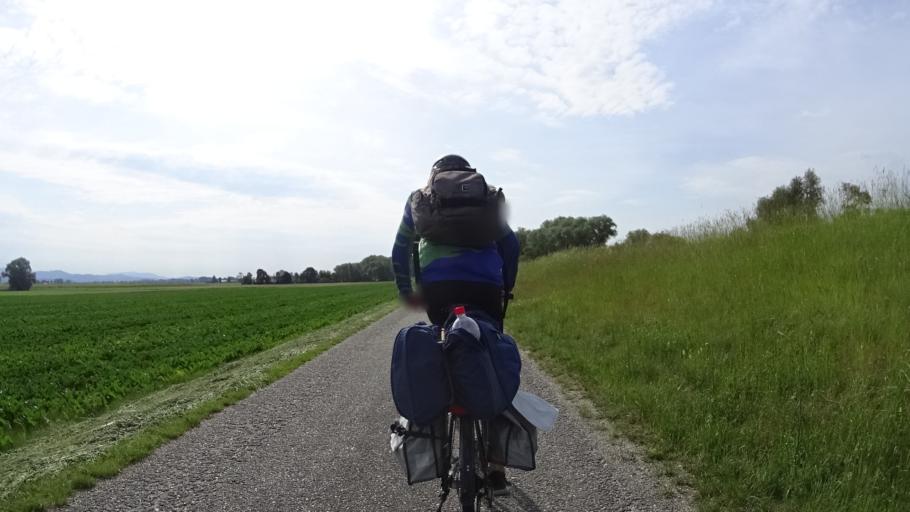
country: DE
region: Bavaria
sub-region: Lower Bavaria
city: Mariaposching
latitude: 48.8316
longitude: 12.7858
